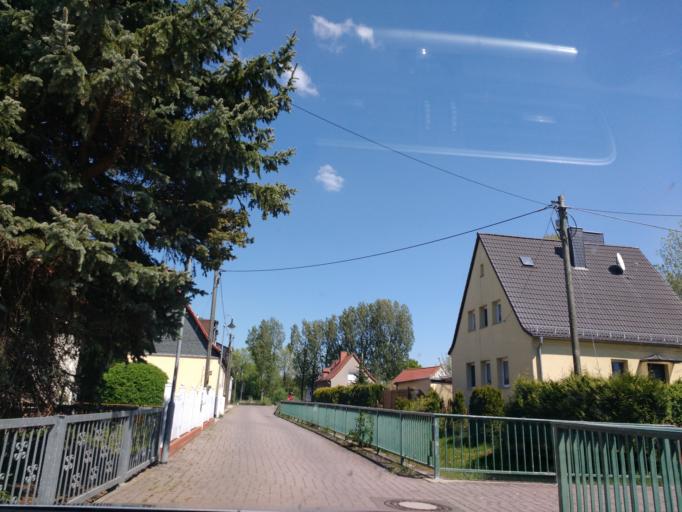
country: DE
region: Saxony-Anhalt
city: Peissen
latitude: 51.5025
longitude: 12.0538
